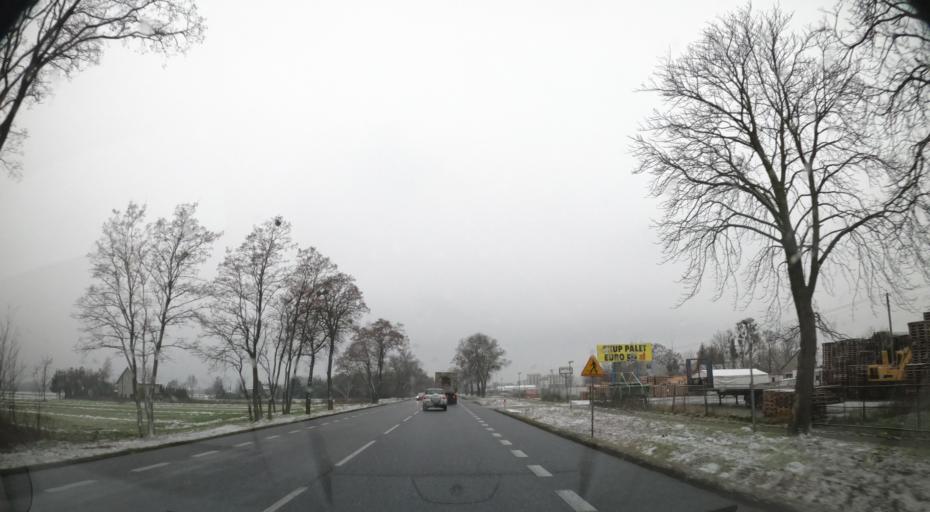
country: PL
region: Masovian Voivodeship
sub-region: Powiat sochaczewski
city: Teresin
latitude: 52.2205
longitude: 20.3368
